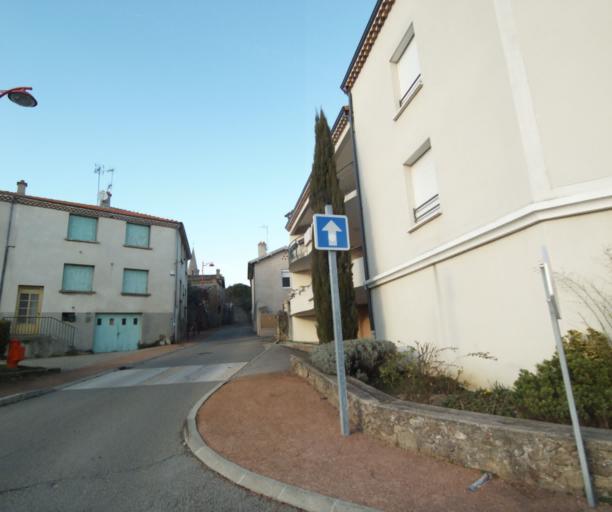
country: FR
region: Rhone-Alpes
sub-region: Departement de l'Ardeche
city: Davezieux
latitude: 45.2535
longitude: 4.7058
